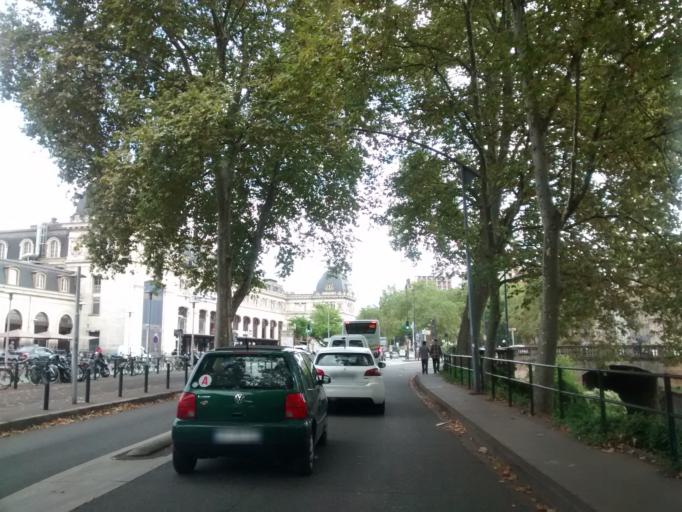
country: FR
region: Midi-Pyrenees
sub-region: Departement de la Haute-Garonne
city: Toulouse
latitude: 43.6123
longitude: 1.4525
